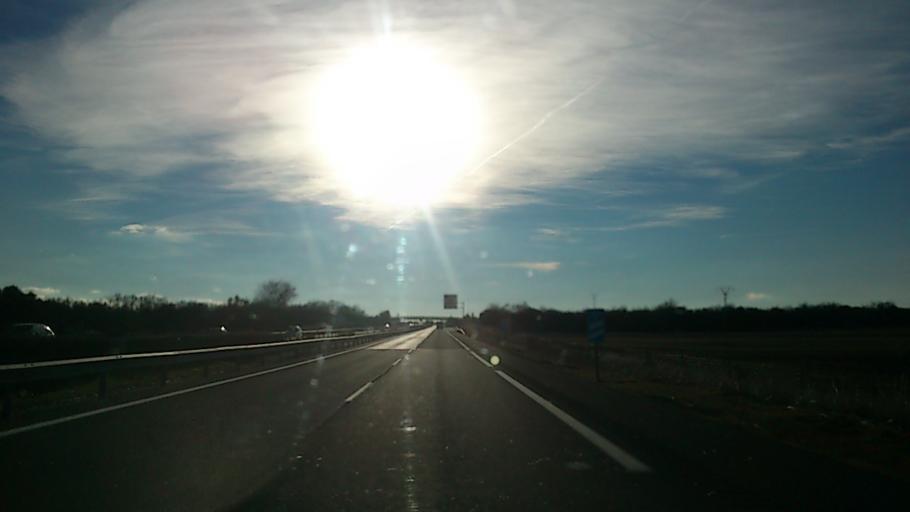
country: ES
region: Castille-La Mancha
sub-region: Provincia de Guadalajara
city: Mirabueno
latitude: 40.9169
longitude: -2.7322
